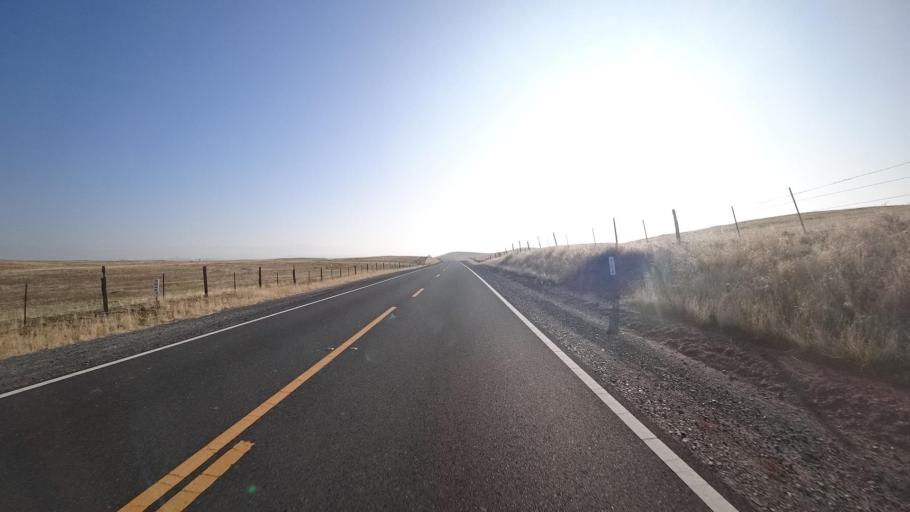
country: US
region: California
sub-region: Tulare County
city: Richgrove
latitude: 35.7504
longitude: -118.9957
